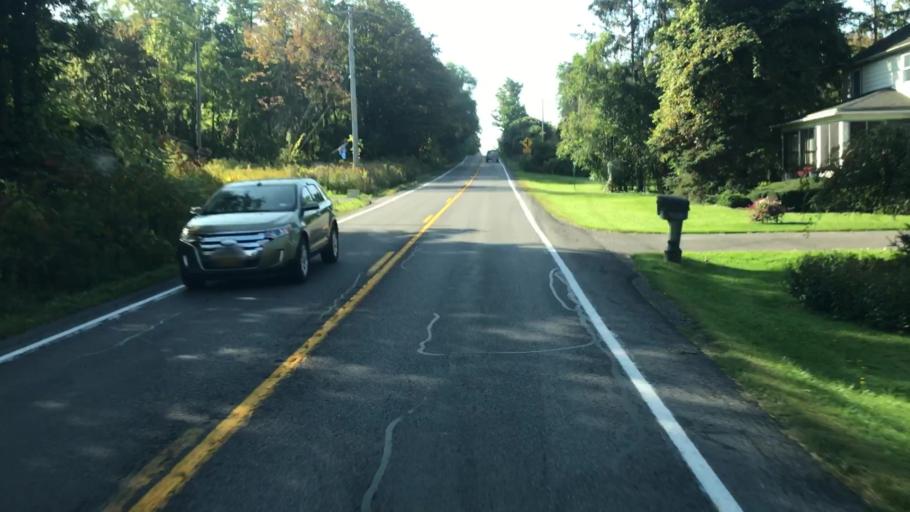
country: US
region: New York
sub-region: Onondaga County
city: Skaneateles
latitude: 42.9851
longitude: -76.4285
